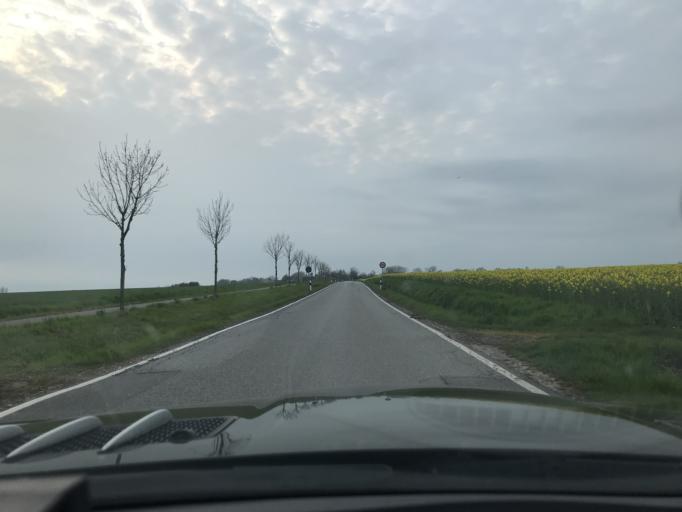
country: DE
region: Schleswig-Holstein
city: Burg auf Fehmarn
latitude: 54.4196
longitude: 11.2631
